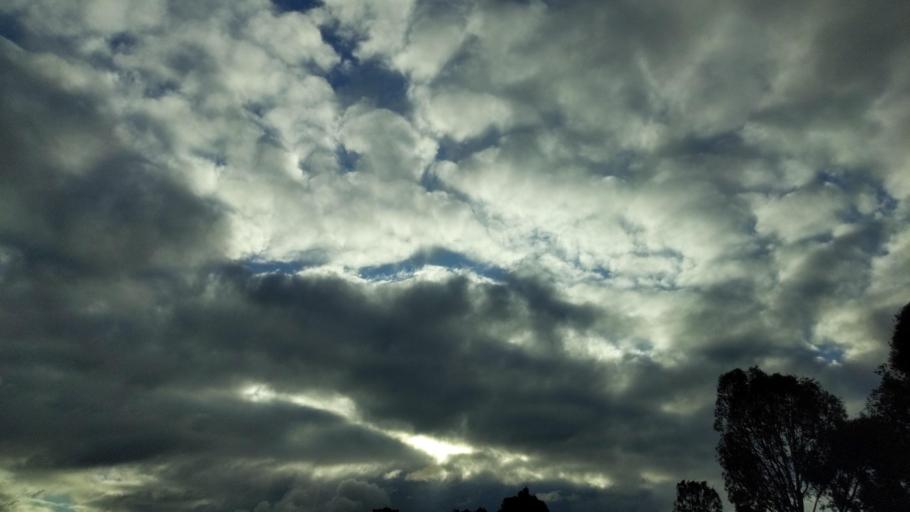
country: AU
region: New South Wales
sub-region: Wagga Wagga
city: Wagga Wagga
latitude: -35.0697
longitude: 147.3799
